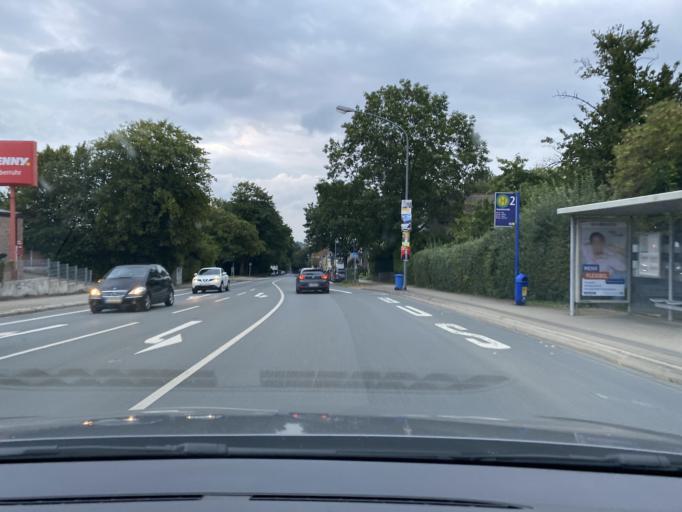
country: DE
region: North Rhine-Westphalia
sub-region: Regierungsbezirk Dusseldorf
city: Essen
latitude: 51.4337
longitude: 7.0778
